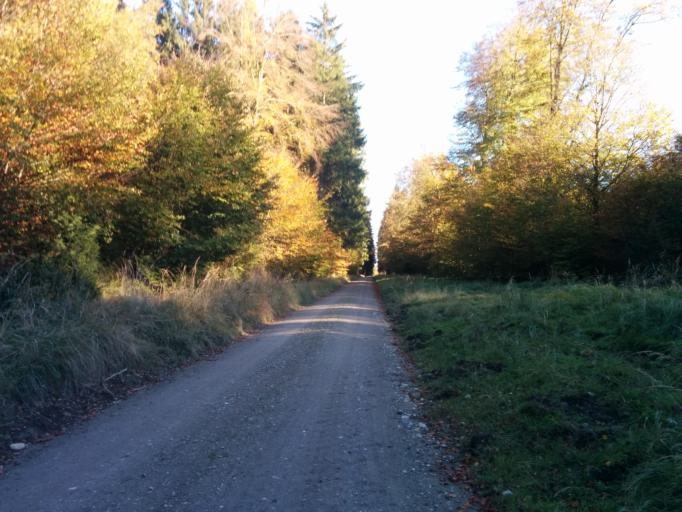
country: DE
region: Bavaria
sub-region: Upper Bavaria
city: Schaftlarn
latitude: 48.0170
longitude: 11.4557
